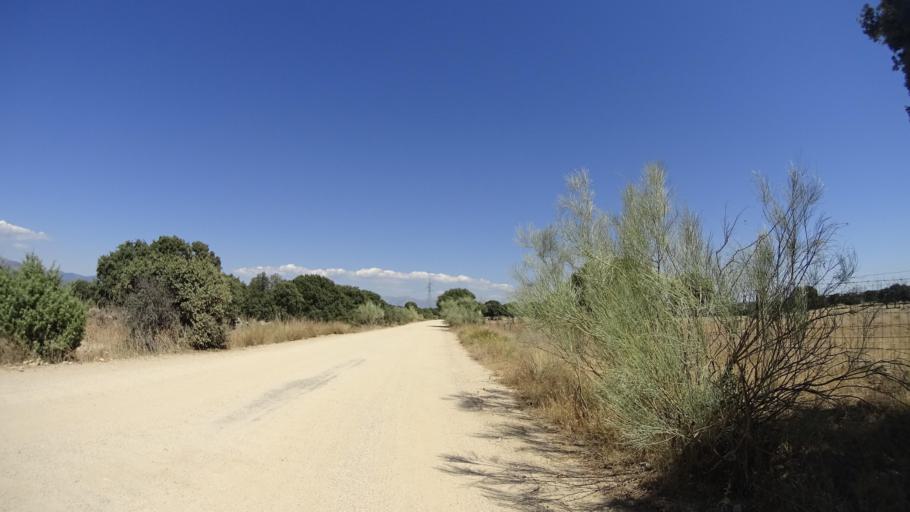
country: ES
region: Madrid
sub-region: Provincia de Madrid
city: Colmenarejo
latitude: 40.5341
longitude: -4.0110
